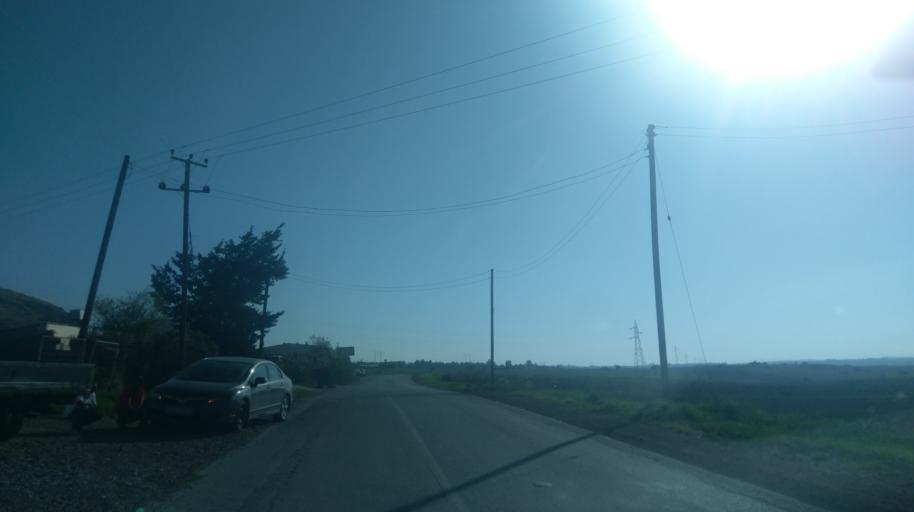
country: CY
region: Keryneia
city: Kyrenia
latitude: 35.2889
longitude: 33.2880
